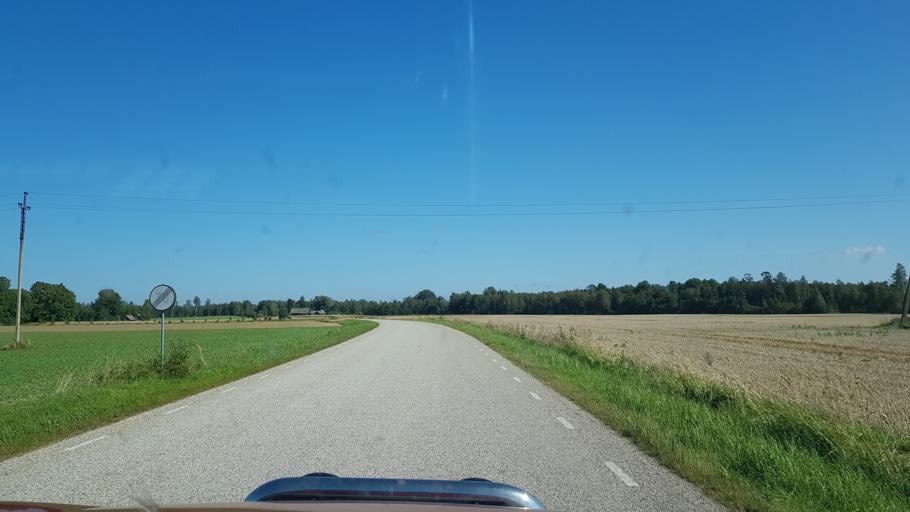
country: EE
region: Polvamaa
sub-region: Raepina vald
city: Rapina
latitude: 58.2125
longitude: 27.2686
